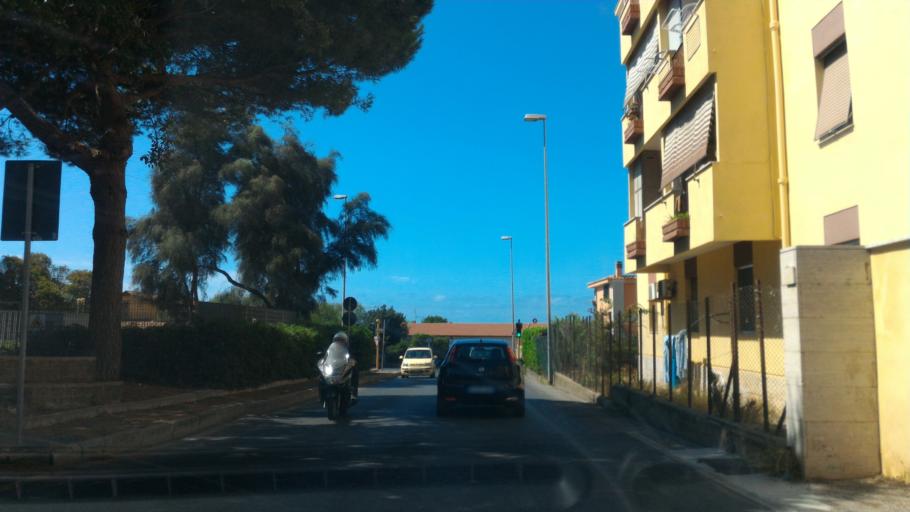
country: IT
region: Latium
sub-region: Citta metropolitana di Roma Capitale
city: Civitavecchia
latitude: 42.0814
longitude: 11.8092
